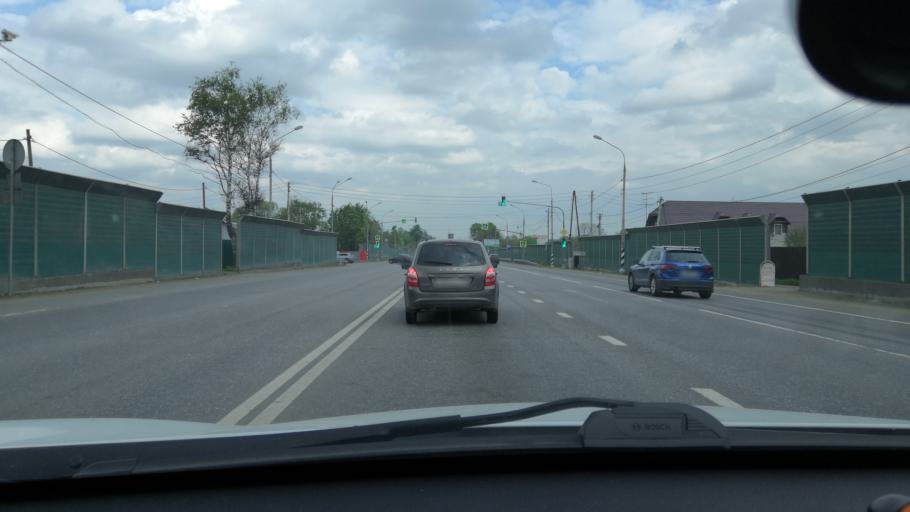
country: RU
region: Moskovskaya
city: Lozhki
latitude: 56.0934
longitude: 37.1088
